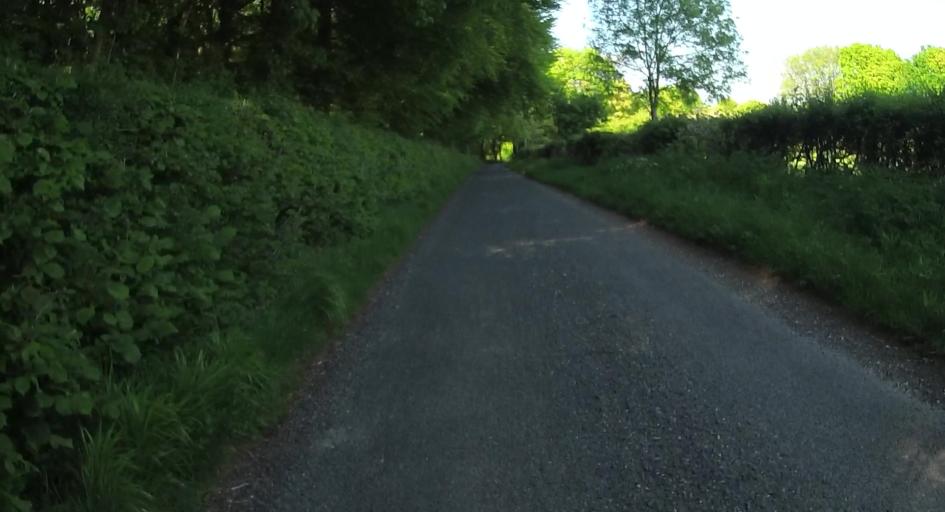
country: GB
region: England
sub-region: Hampshire
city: Overton
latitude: 51.1719
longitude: -1.2175
